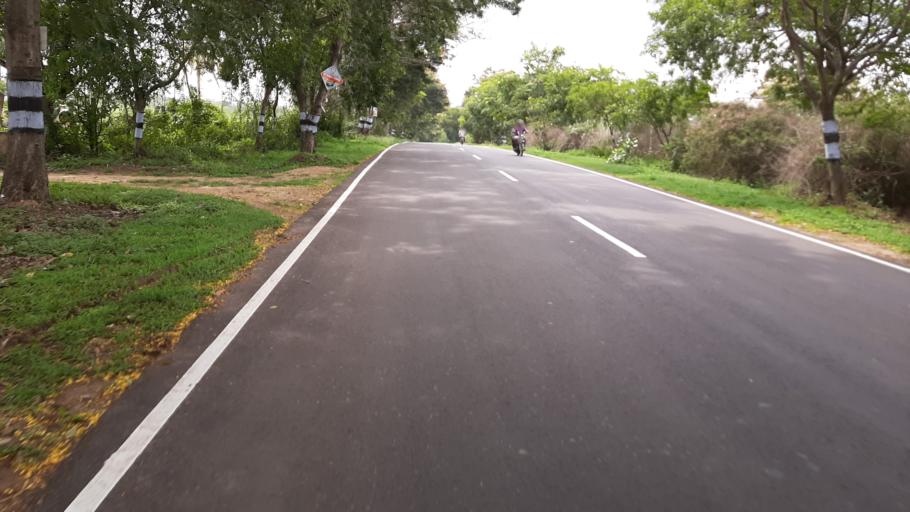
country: IN
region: Tamil Nadu
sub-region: Krishnagiri
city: Denkanikota
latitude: 12.5394
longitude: 77.7654
